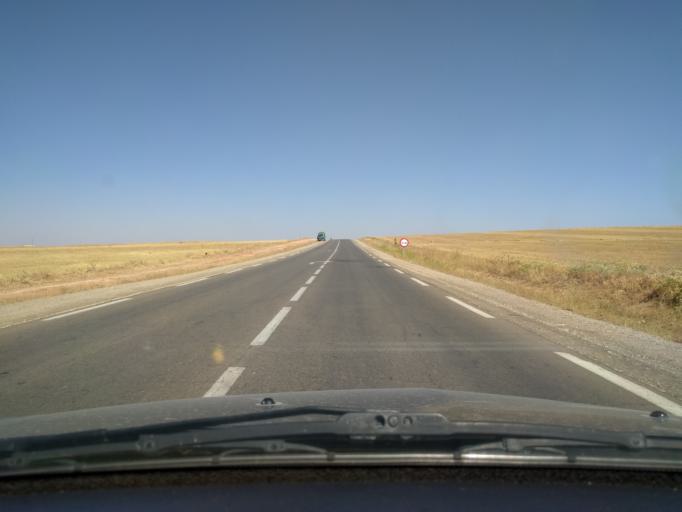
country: DZ
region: Tiaret
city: Frenda
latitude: 34.8835
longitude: 1.1900
